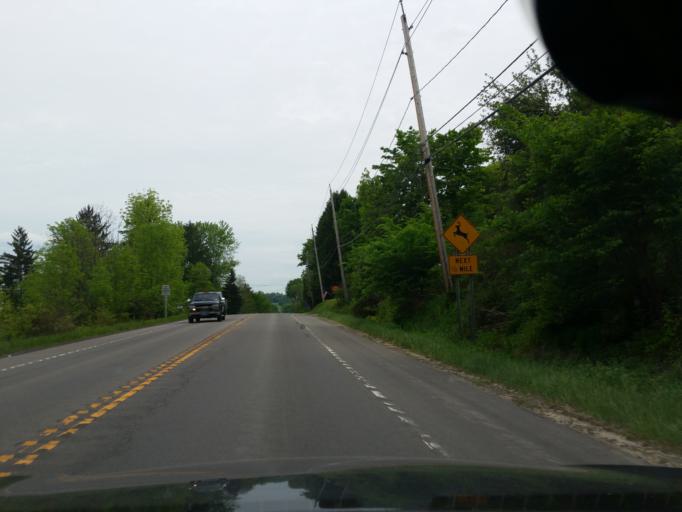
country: US
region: New York
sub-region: Chautauqua County
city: Lakewood
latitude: 42.1261
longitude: -79.3931
